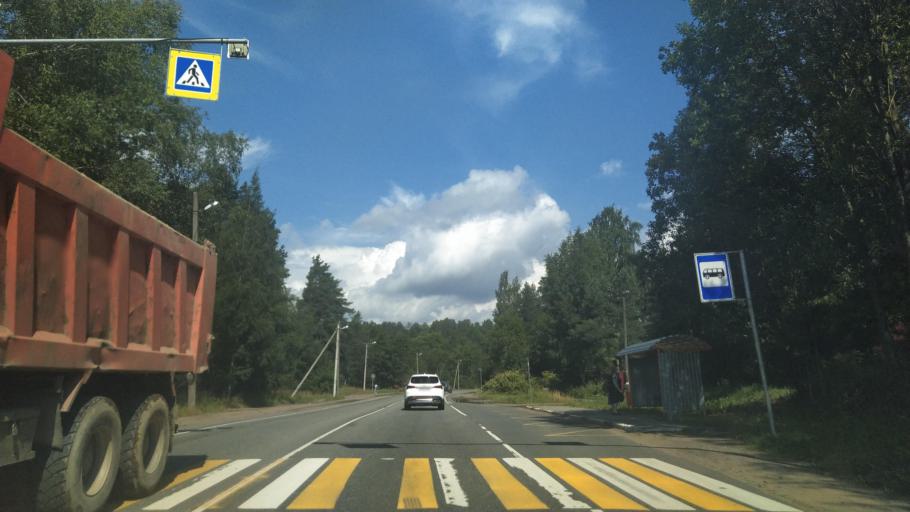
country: RU
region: Leningrad
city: Toksovo
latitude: 60.1526
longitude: 30.5221
